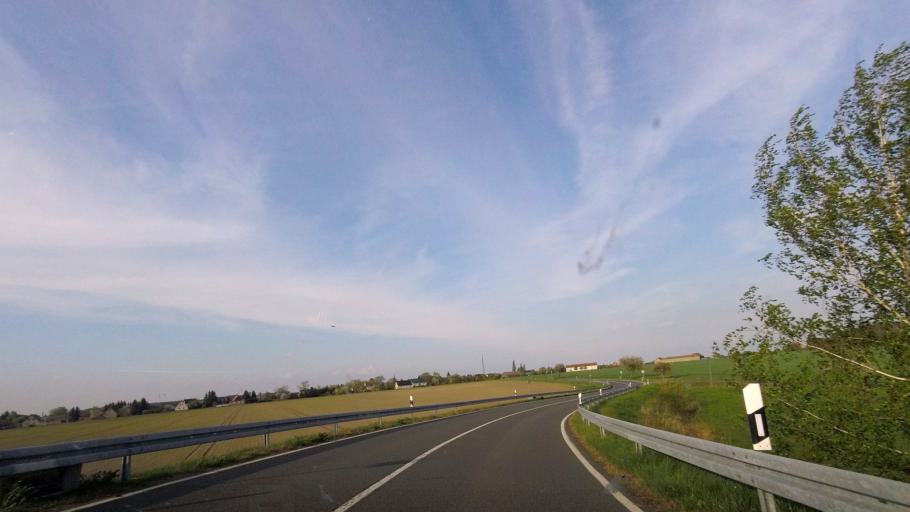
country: DE
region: Saxony-Anhalt
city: Zahna
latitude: 51.9426
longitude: 12.8352
